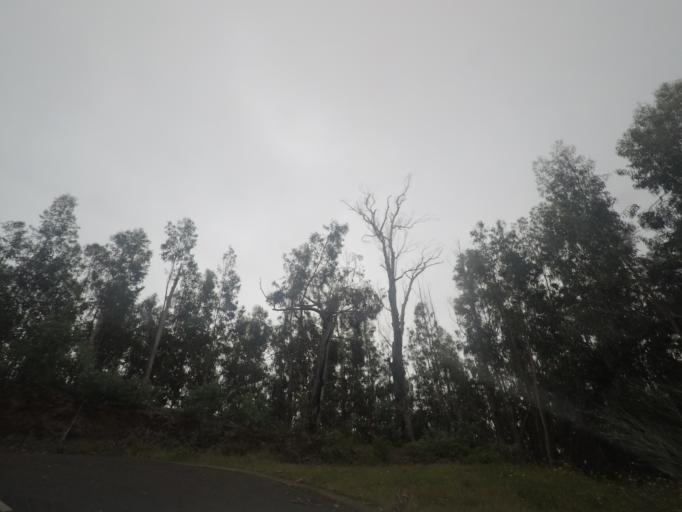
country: PT
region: Madeira
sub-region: Camara de Lobos
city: Curral das Freiras
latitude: 32.6970
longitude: -16.9387
